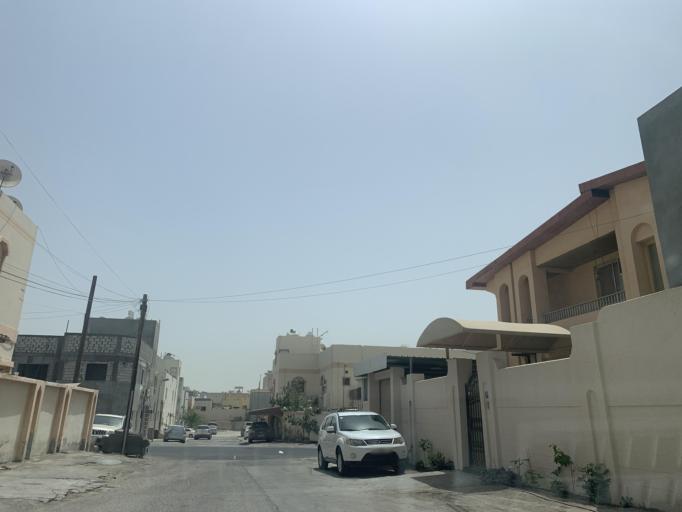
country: BH
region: Central Governorate
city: Madinat Hamad
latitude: 26.1488
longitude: 50.5188
